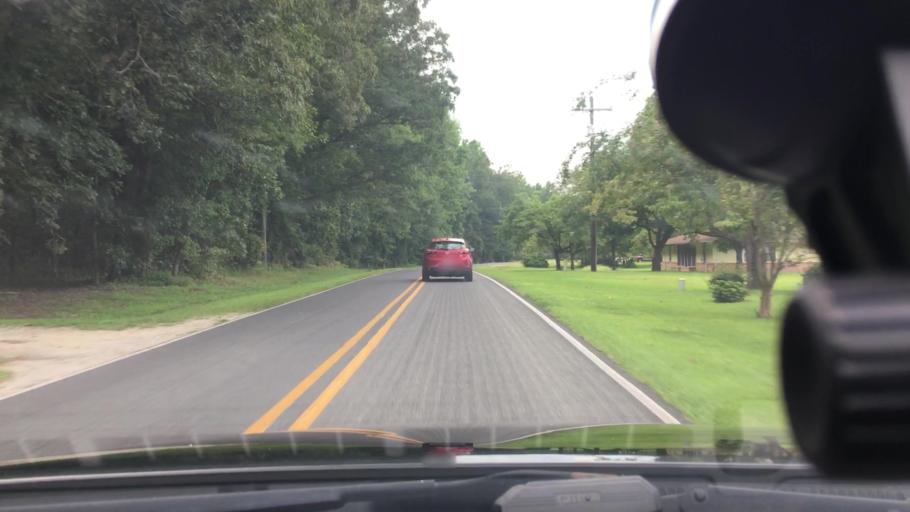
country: US
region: North Carolina
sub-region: Craven County
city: New Bern
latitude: 35.1790
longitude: -77.0552
